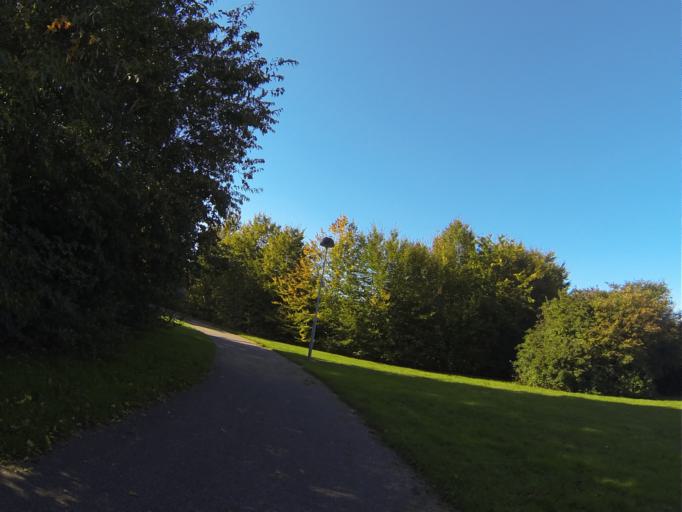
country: SE
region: Skane
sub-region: Eslovs Kommun
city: Eslov
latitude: 55.7226
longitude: 13.3483
